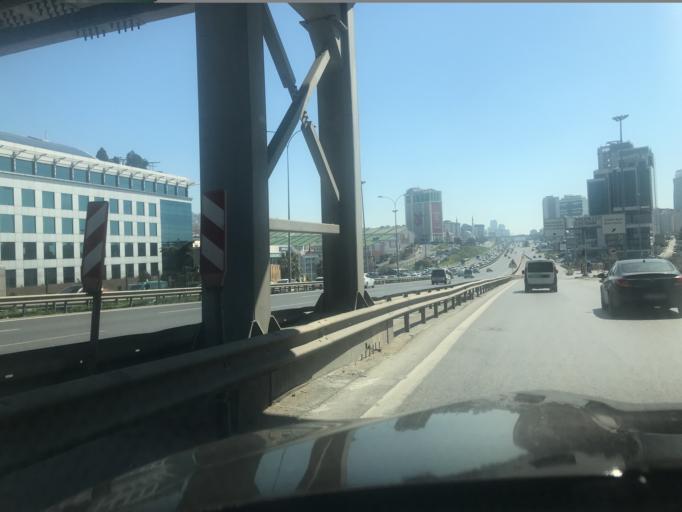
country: TR
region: Istanbul
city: Maltepe
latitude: 40.9446
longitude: 29.1278
